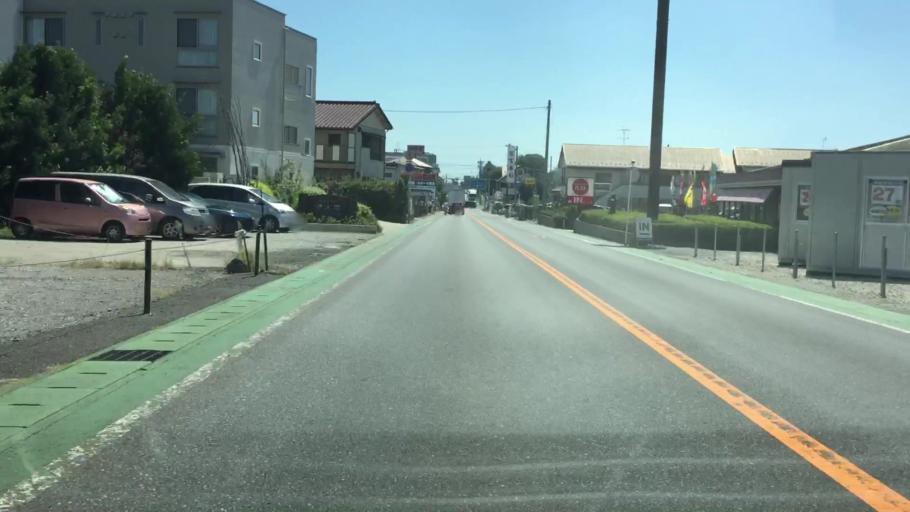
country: JP
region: Chiba
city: Funabashi
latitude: 35.7300
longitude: 139.9595
